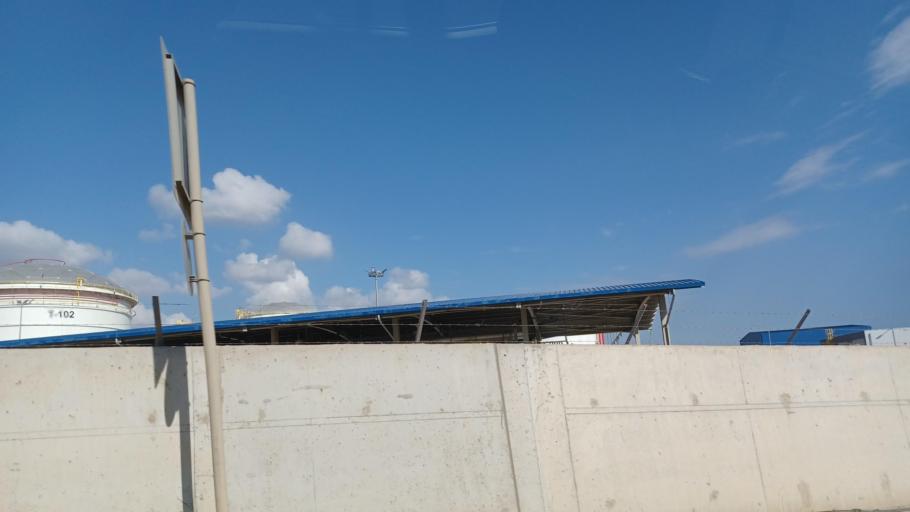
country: CY
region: Limassol
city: Pyrgos
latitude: 34.7249
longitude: 33.3101
